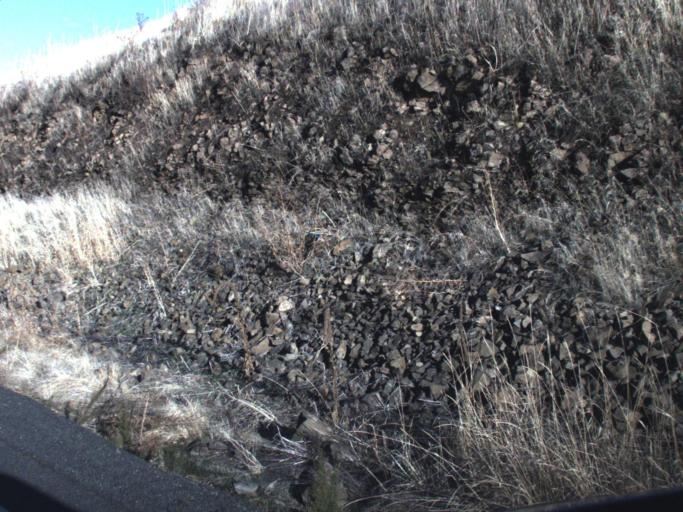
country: US
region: Washington
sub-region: Whitman County
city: Pullman
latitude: 46.7217
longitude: -117.2849
